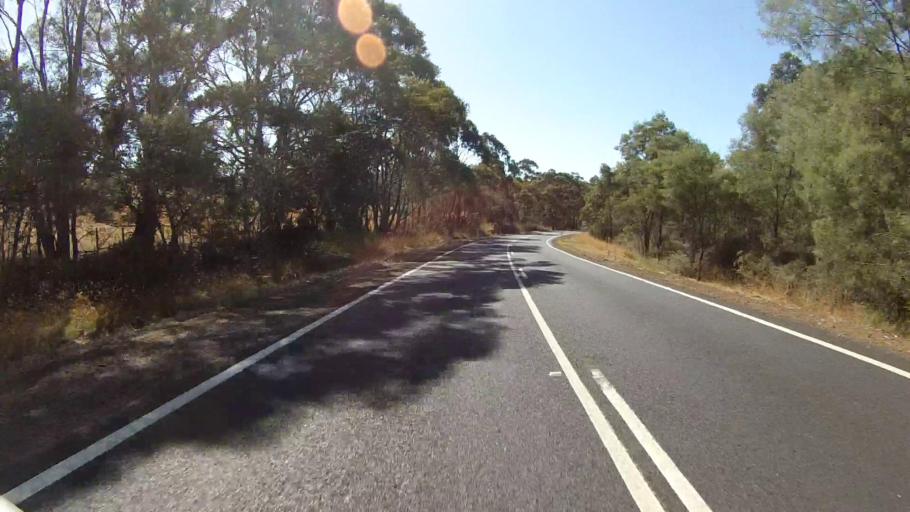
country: AU
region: Tasmania
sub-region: Sorell
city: Sorell
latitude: -42.4108
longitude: 147.9337
